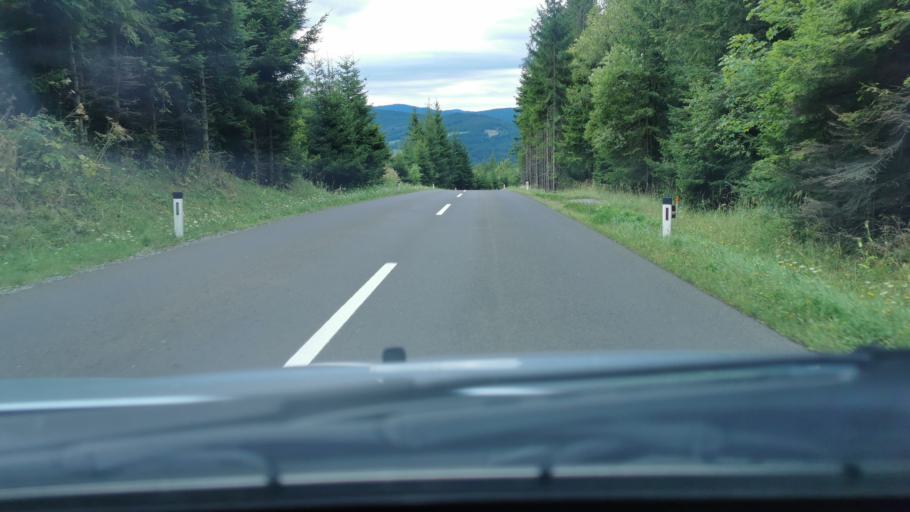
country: AT
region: Styria
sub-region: Politischer Bezirk Weiz
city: Fischbach
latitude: 47.4089
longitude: 15.6611
